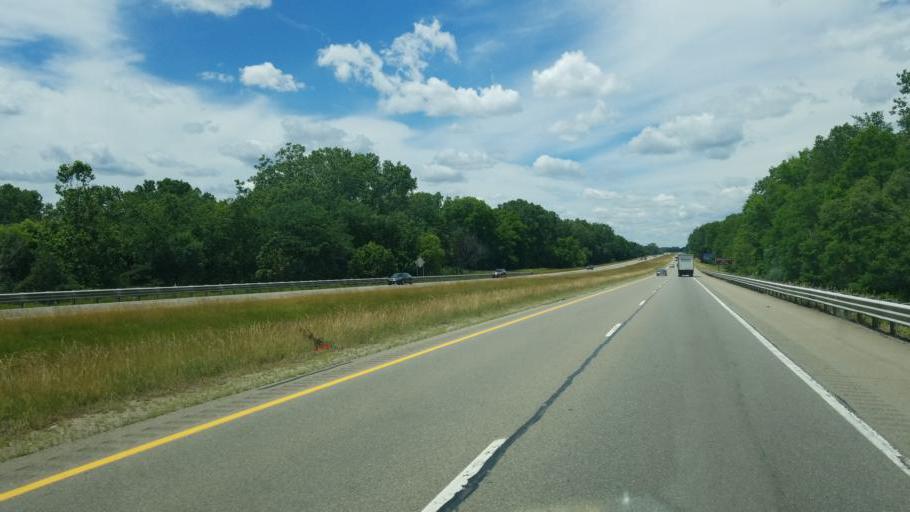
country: US
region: Michigan
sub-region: Ingham County
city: Holt
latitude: 42.6614
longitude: -84.5655
